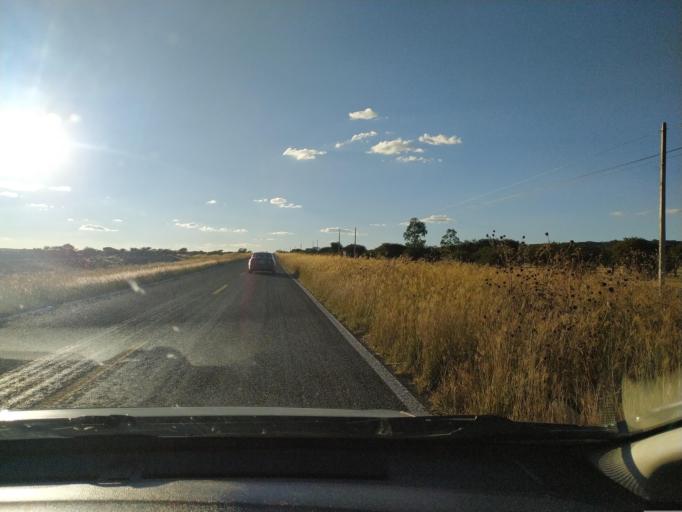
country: MX
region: Jalisco
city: San Diego de Alejandria
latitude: 21.0052
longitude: -102.0692
